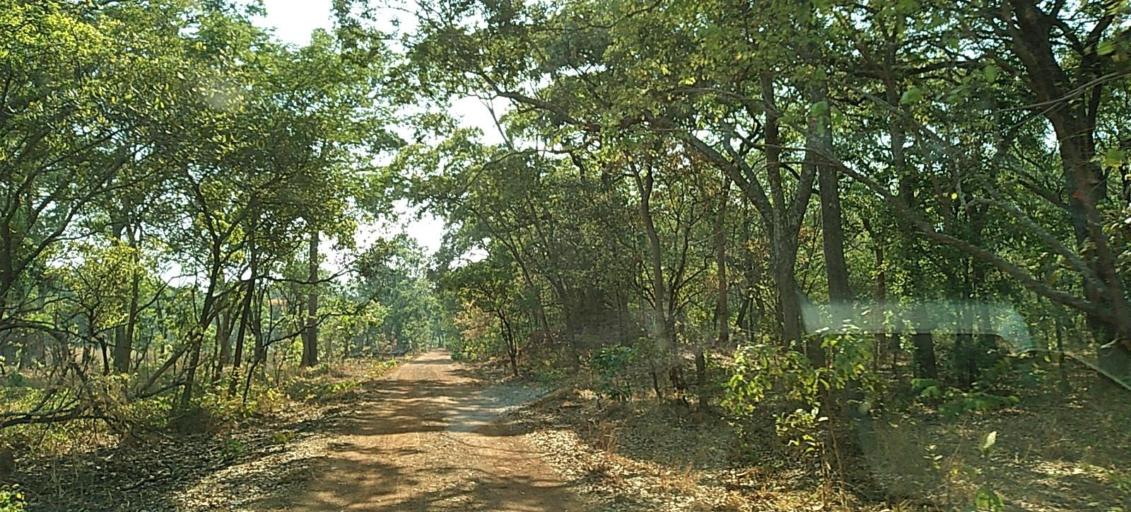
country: ZM
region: Copperbelt
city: Kalulushi
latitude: -13.0063
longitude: 27.7326
